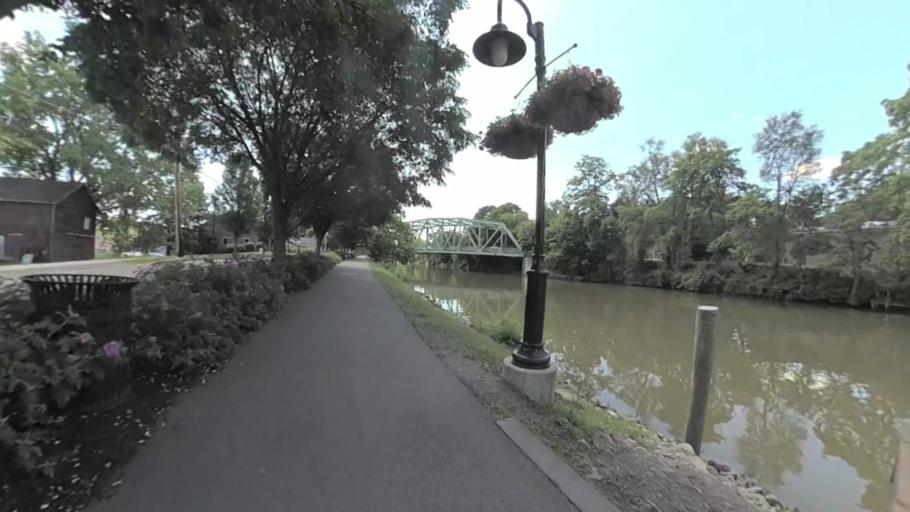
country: US
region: New York
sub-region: Monroe County
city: Pittsford
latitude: 43.0903
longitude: -77.5116
